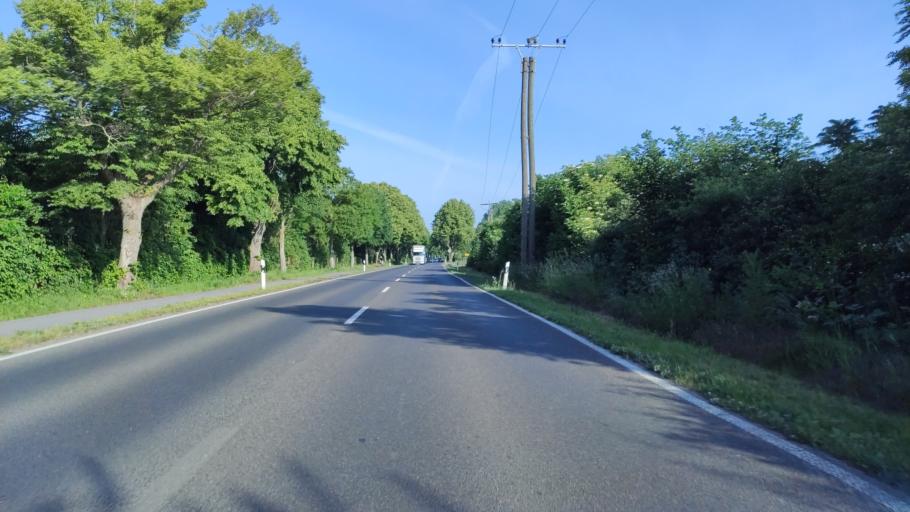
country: DE
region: North Rhine-Westphalia
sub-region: Regierungsbezirk Dusseldorf
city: Dormagen
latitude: 51.1038
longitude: 6.7925
